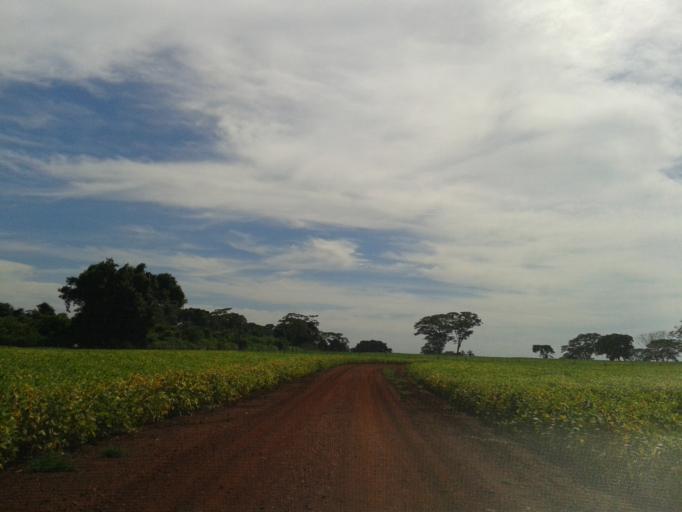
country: BR
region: Minas Gerais
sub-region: Capinopolis
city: Capinopolis
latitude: -18.6369
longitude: -49.7206
